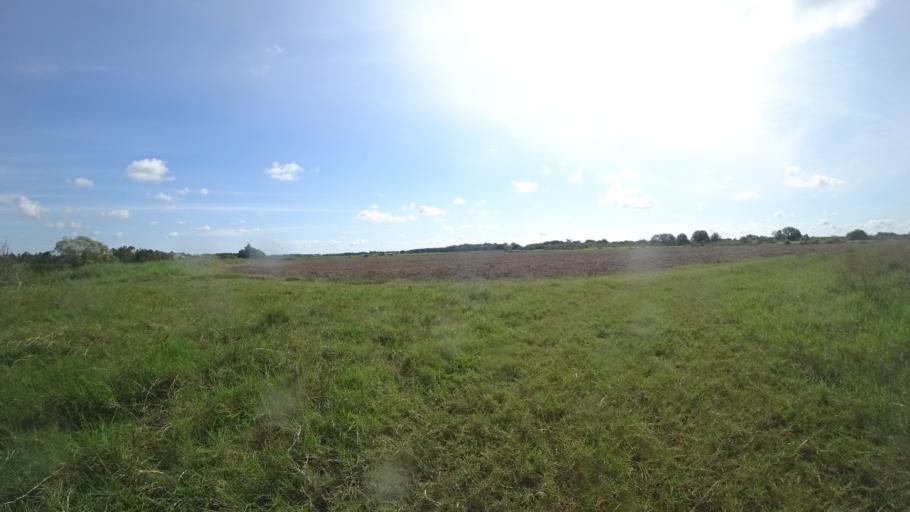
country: US
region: Florida
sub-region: Sarasota County
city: The Meadows
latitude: 27.4520
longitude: -82.3201
